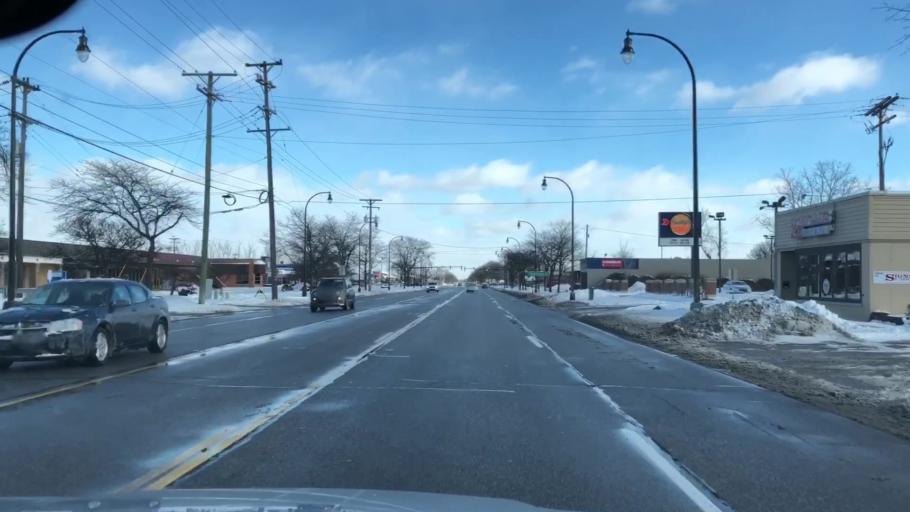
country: US
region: Michigan
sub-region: Wayne County
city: Livonia
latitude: 42.3682
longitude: -83.3752
